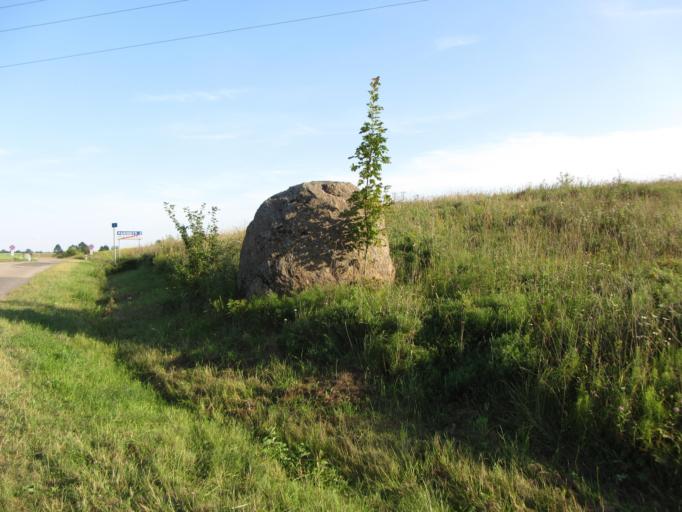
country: LT
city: Ignalina
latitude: 55.3422
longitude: 26.3351
